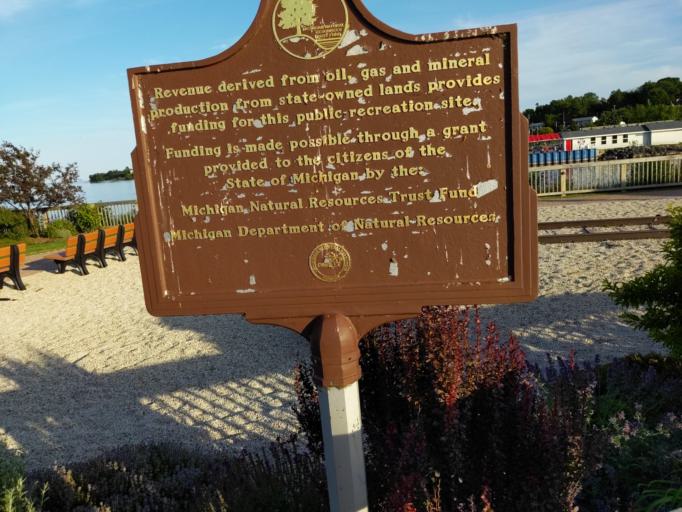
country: US
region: Michigan
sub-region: Mackinac County
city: Saint Ignace
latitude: 45.8657
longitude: -84.7167
